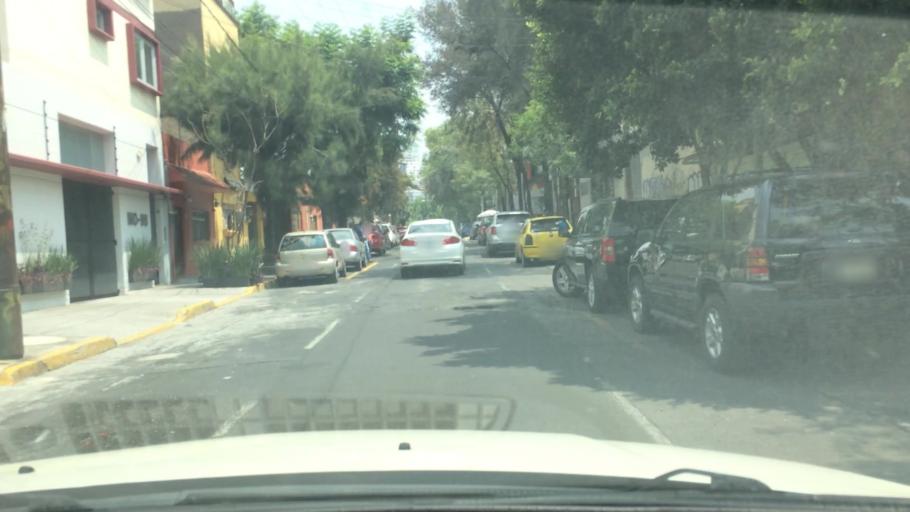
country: MX
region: Mexico City
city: Alvaro Obregon
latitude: 19.3677
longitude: -99.1919
